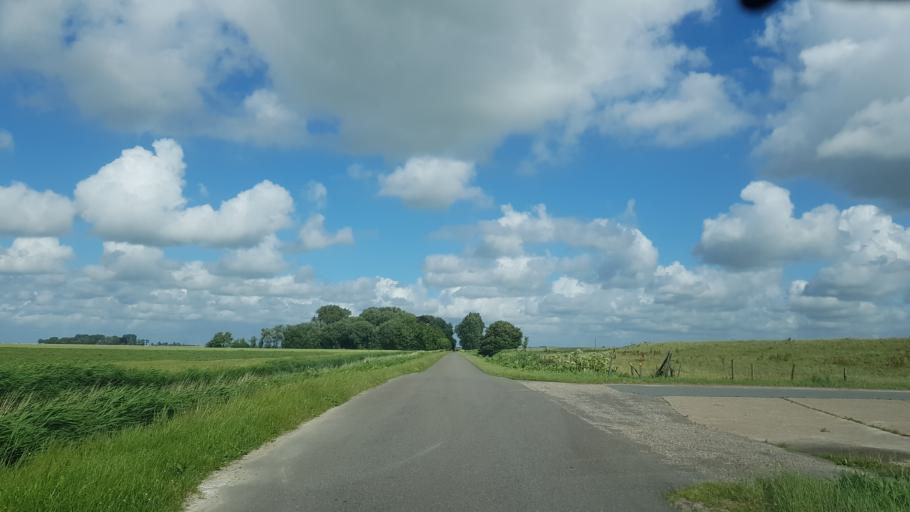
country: NL
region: Groningen
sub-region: Gemeente Winsum
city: Winsum
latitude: 53.4068
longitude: 6.5225
